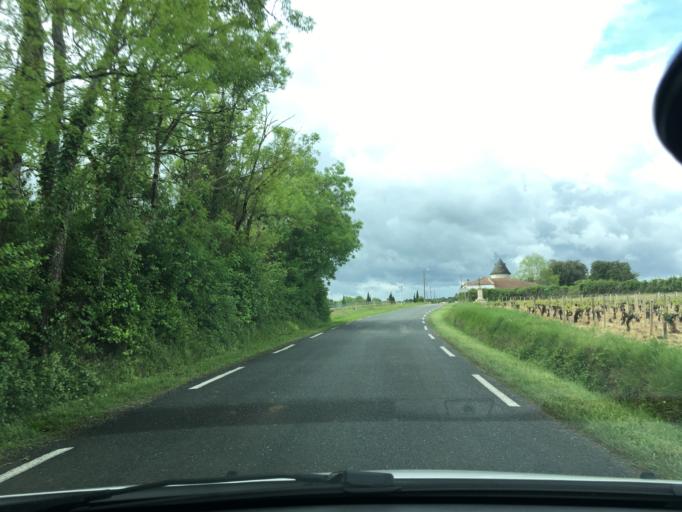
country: FR
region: Aquitaine
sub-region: Departement de la Gironde
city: Vertheuil
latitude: 45.3199
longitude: -0.8358
